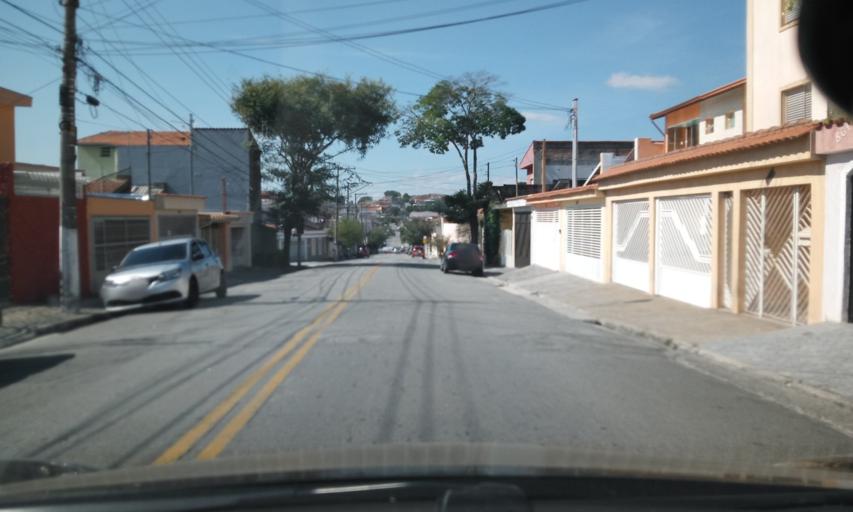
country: BR
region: Sao Paulo
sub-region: Sao Bernardo Do Campo
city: Sao Bernardo do Campo
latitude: -23.7179
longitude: -46.5761
